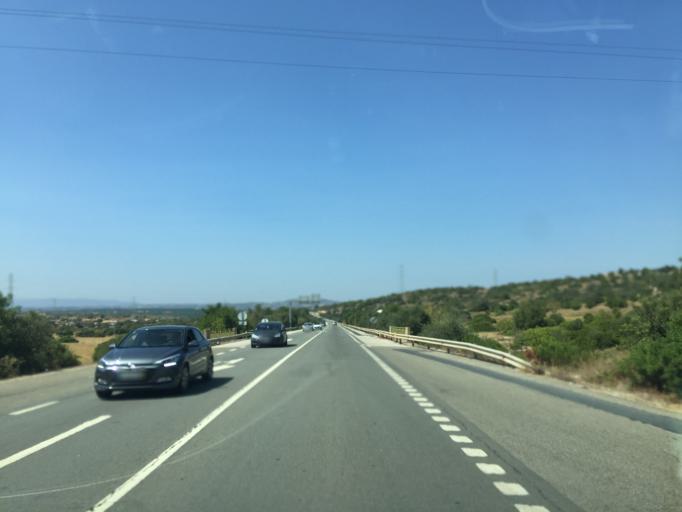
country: PT
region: Faro
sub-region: Albufeira
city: Ferreiras
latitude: 37.1692
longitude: -8.2555
